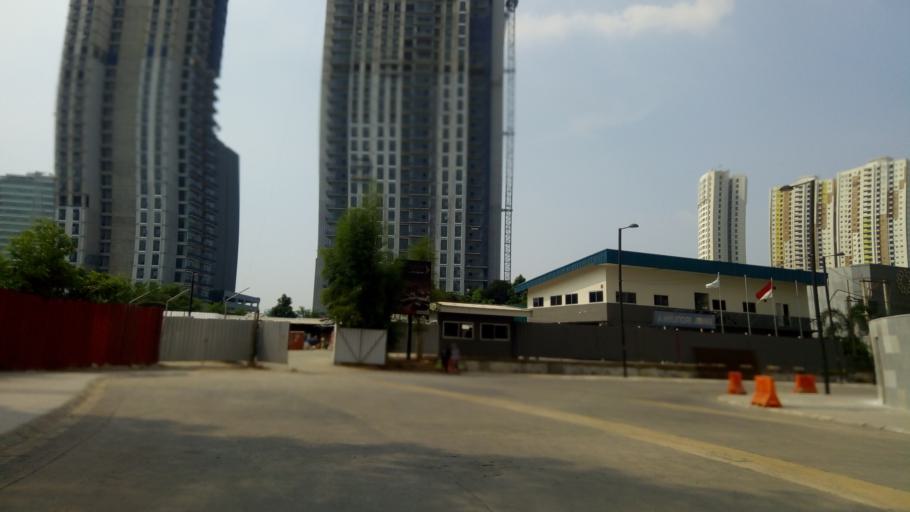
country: ID
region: Jakarta Raya
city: Jakarta
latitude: -6.2168
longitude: 106.8341
